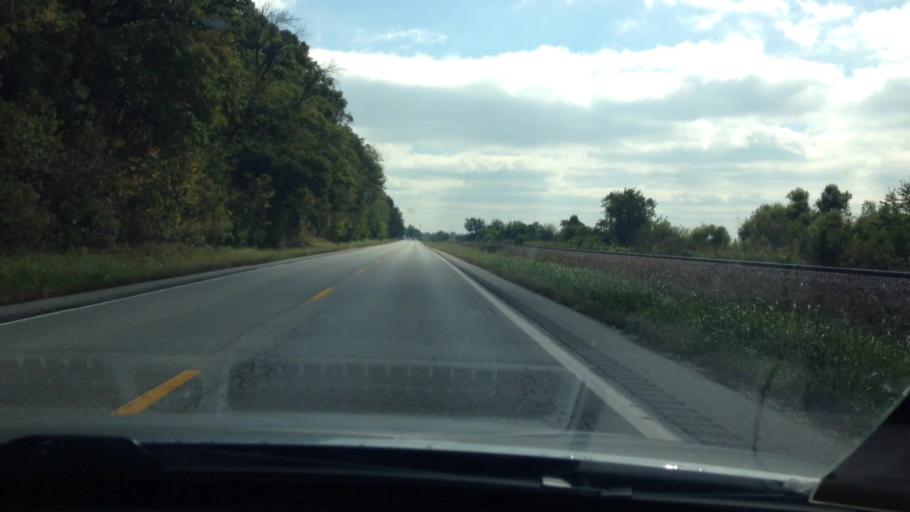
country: US
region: Kansas
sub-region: Leavenworth County
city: Lansing
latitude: 39.2907
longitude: -94.8407
